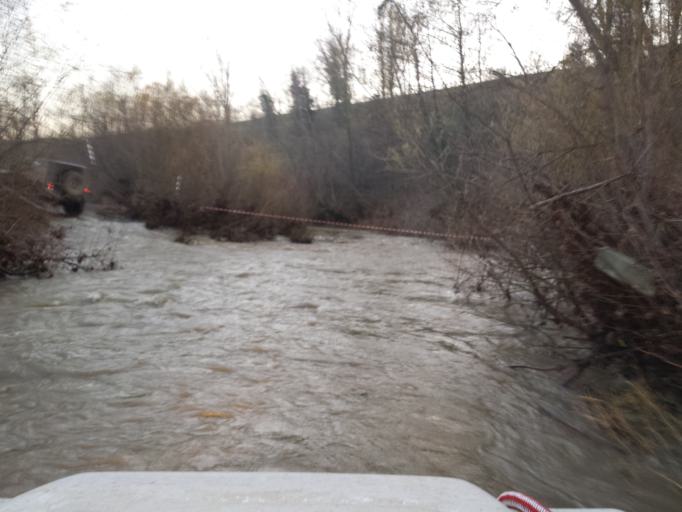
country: IT
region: Friuli Venezia Giulia
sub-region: Provincia di Udine
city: Corno di Rosazzo
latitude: 46.0006
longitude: 13.4606
